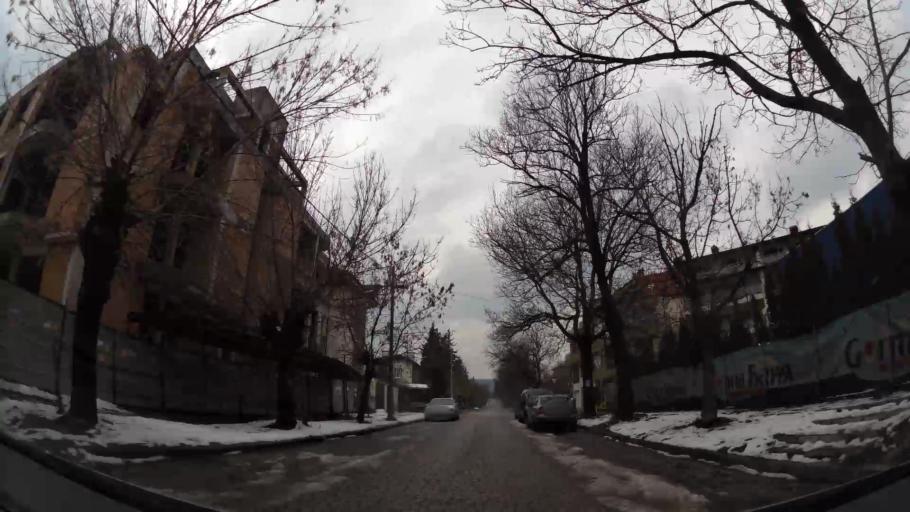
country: BG
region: Sofiya
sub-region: Obshtina Bozhurishte
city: Bozhurishte
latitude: 42.6769
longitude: 23.2354
